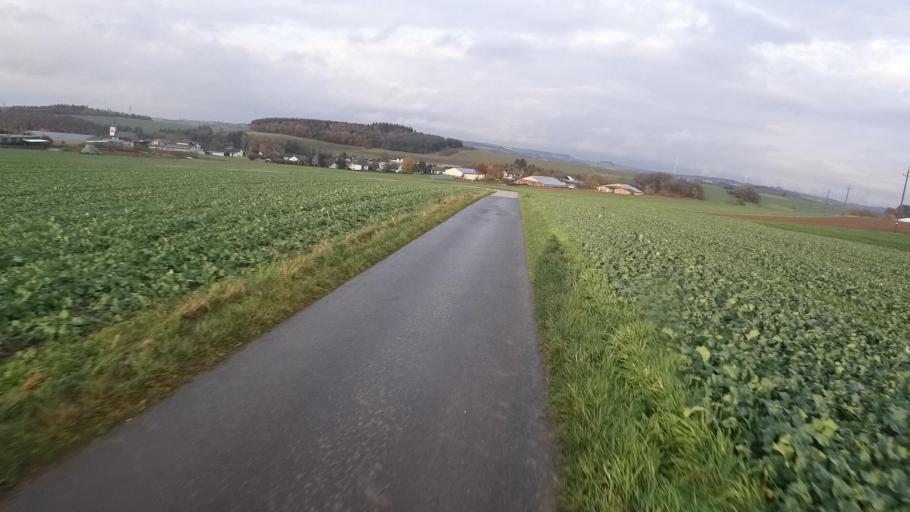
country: DE
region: Rheinland-Pfalz
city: Bickenbach
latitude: 50.1201
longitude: 7.5265
